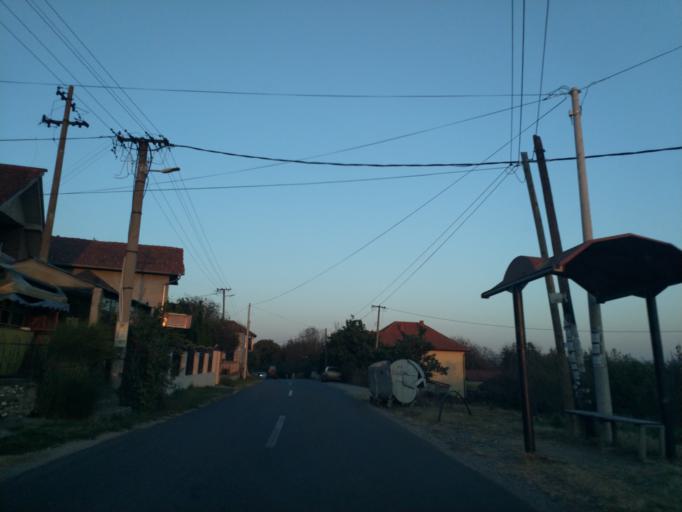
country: RS
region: Central Serbia
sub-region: Rasinski Okrug
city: Krusevac
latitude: 43.6022
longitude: 21.2520
